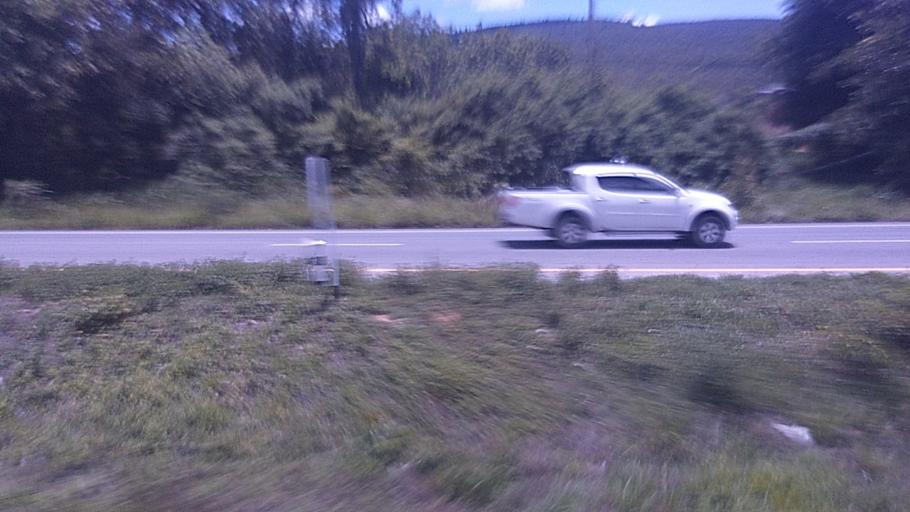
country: TH
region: Chaiyaphum
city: Khon Sawan
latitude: 15.9464
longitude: 102.1723
